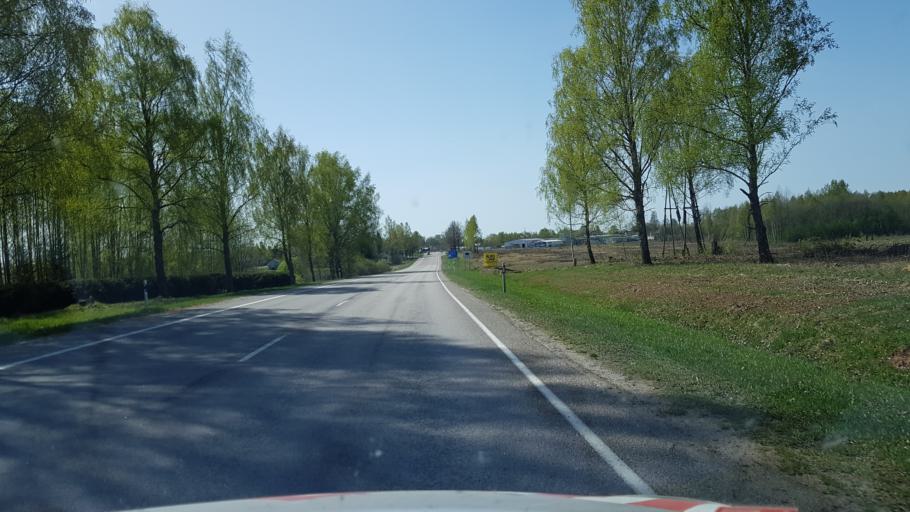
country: EE
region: Valgamaa
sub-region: Valga linn
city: Valga
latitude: 57.7964
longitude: 26.0348
